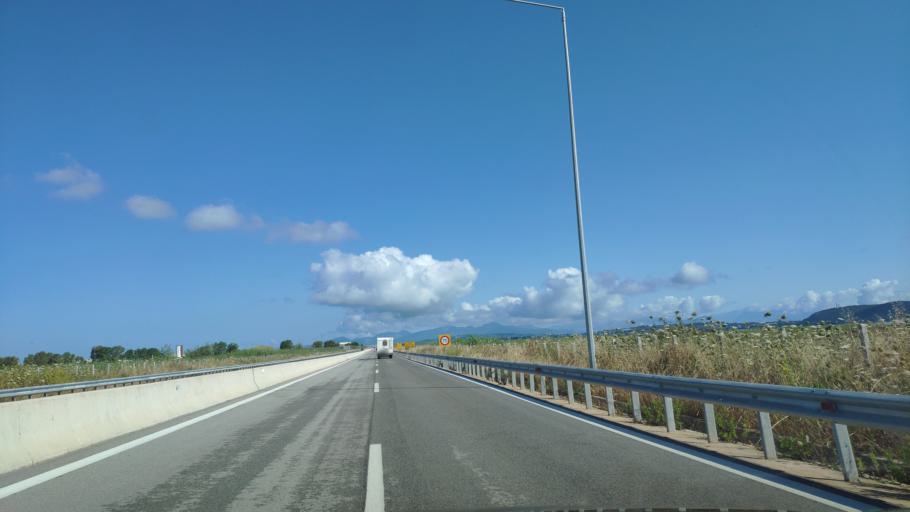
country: GR
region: Epirus
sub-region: Nomos Prevezis
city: Preveza
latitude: 38.9204
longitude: 20.7889
